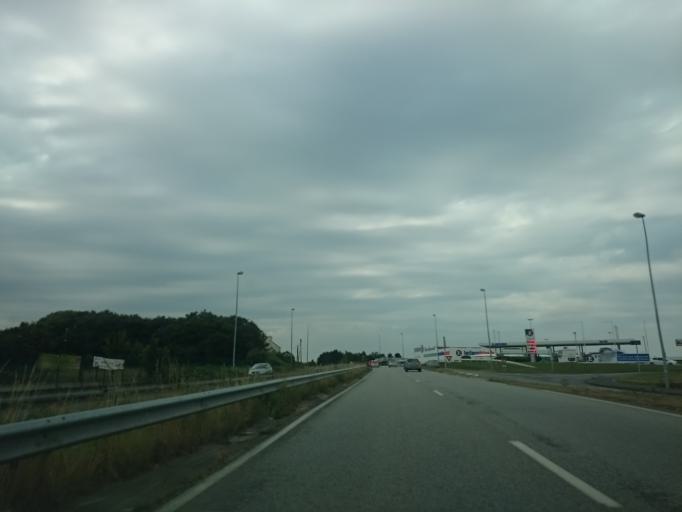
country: FR
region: Brittany
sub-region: Departement du Finistere
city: Guilers
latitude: 48.4255
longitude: -4.5714
